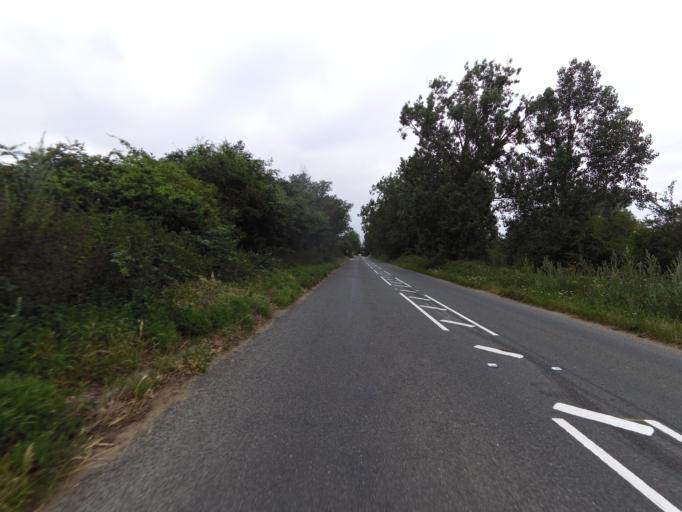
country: GB
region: England
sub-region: Suffolk
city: Bramford
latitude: 52.0944
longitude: 1.0918
